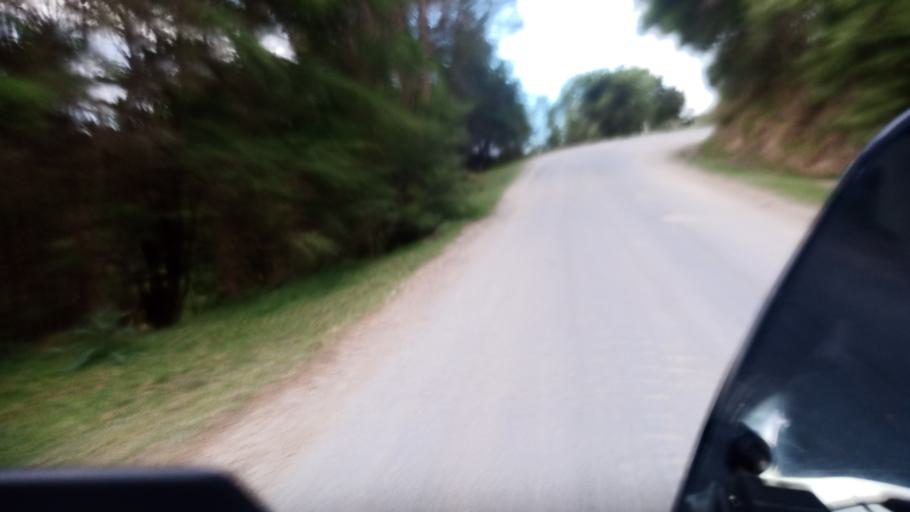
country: NZ
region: Gisborne
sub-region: Gisborne District
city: Gisborne
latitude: -38.4781
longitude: 177.9730
